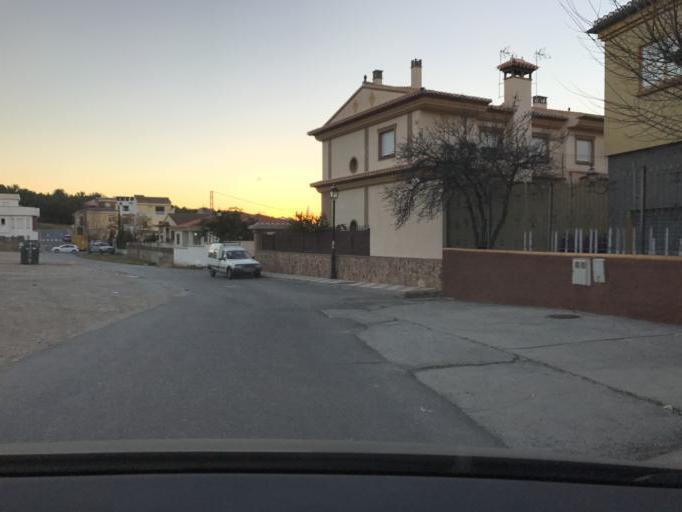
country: ES
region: Andalusia
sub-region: Provincia de Granada
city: Zubia
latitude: 37.1129
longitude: -3.5804
